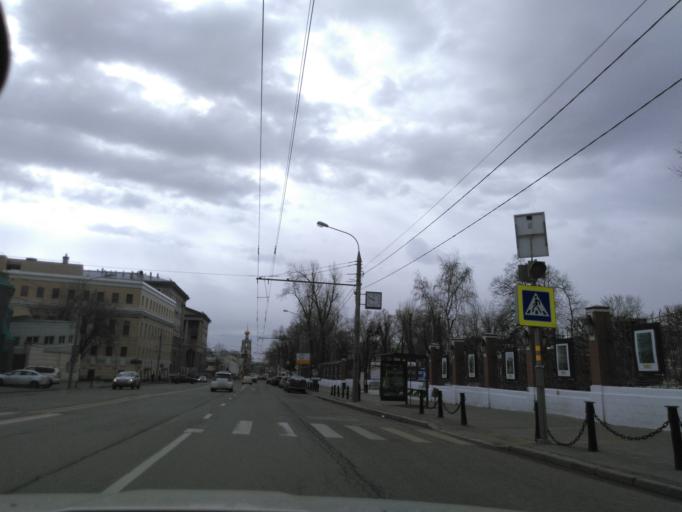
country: RU
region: Moscow
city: Moscow
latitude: 55.7714
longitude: 37.6104
